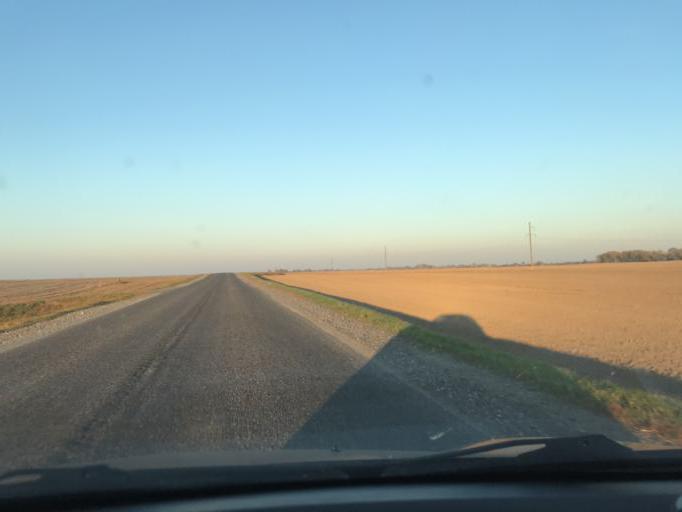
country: BY
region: Gomel
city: Brahin
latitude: 51.8171
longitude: 30.2963
